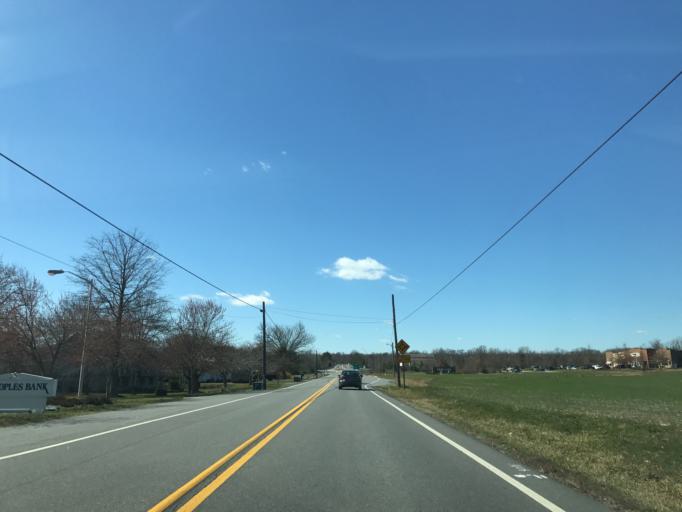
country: US
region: Maryland
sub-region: Queen Anne's County
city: Kingstown
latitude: 39.2630
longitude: -75.8586
